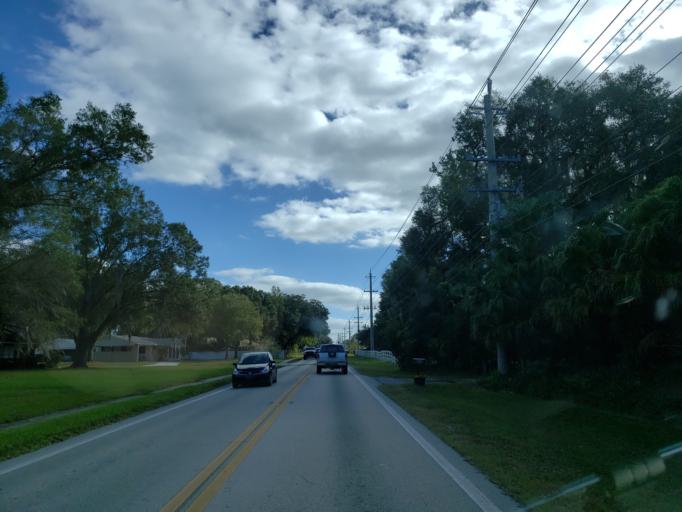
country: US
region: Florida
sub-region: Polk County
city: Medulla
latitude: 27.9749
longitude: -81.9662
